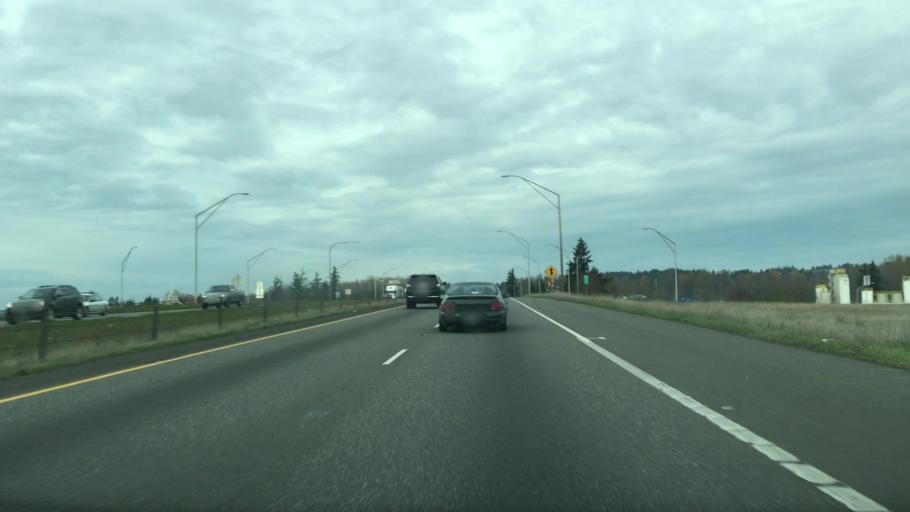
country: US
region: Washington
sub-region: Pierce County
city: Puyallup
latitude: 47.1877
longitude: -122.2827
